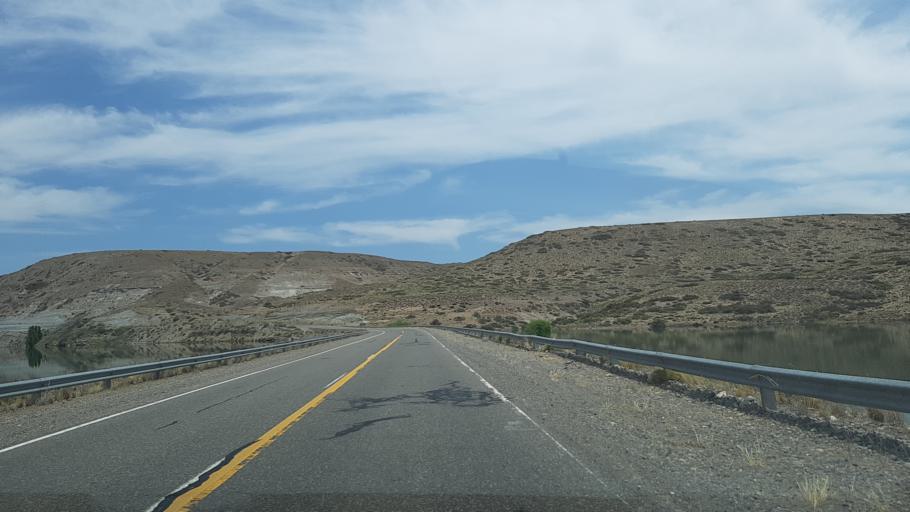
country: AR
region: Neuquen
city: Junin de los Andes
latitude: -40.4387
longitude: -70.6578
